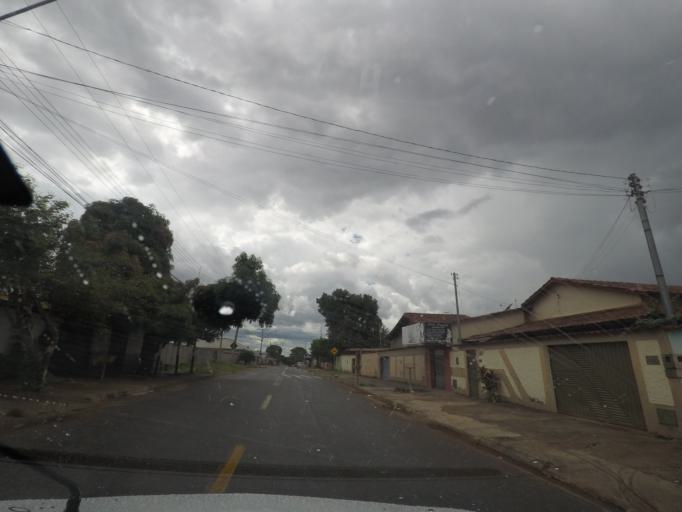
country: BR
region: Goias
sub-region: Goiania
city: Goiania
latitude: -16.7407
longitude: -49.3253
